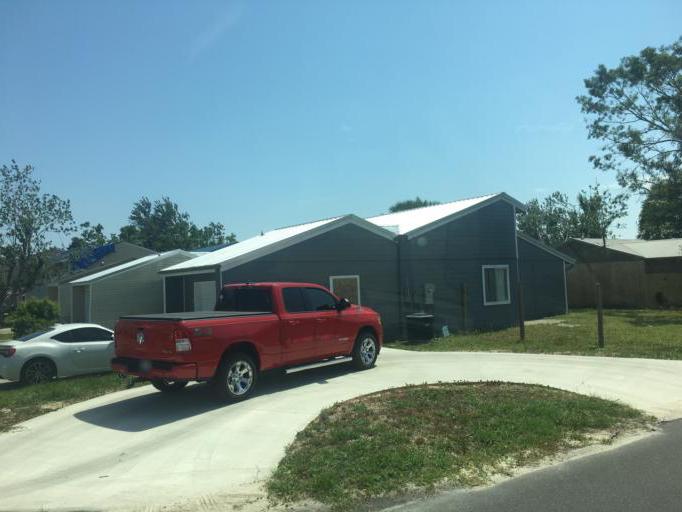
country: US
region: Florida
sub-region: Bay County
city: Lynn Haven
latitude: 30.2219
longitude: -85.6507
